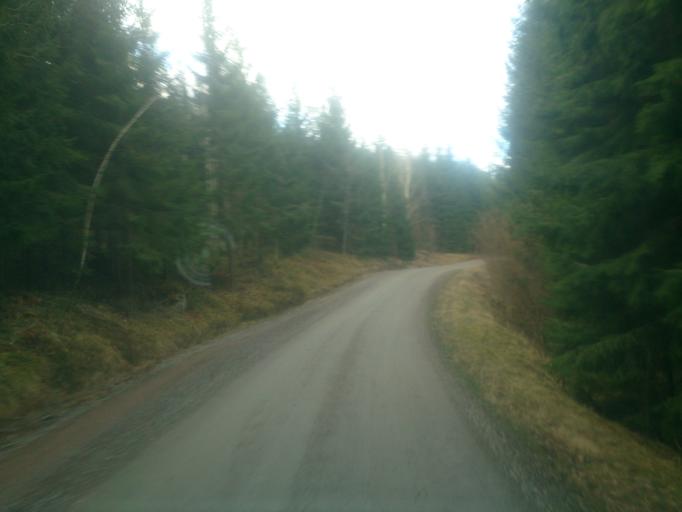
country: SE
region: OEstergoetland
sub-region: Atvidabergs Kommun
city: Atvidaberg
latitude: 58.2002
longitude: 16.1543
